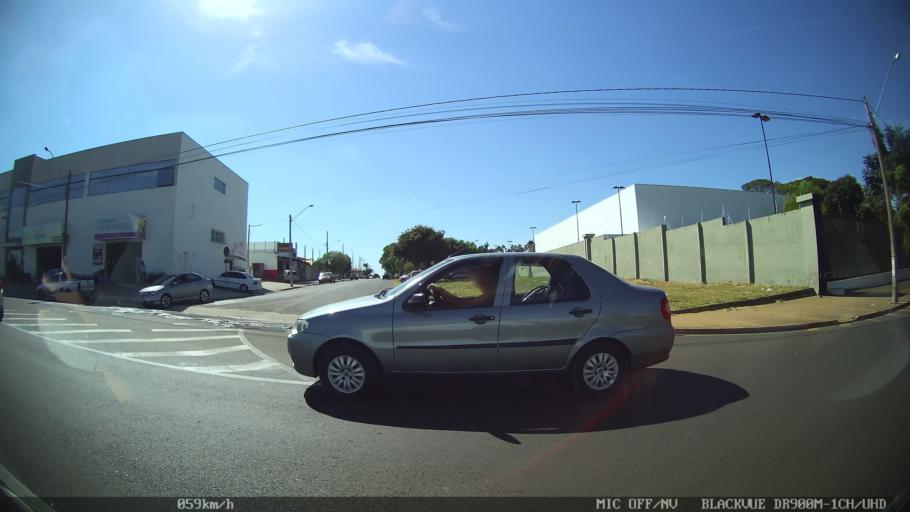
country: BR
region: Sao Paulo
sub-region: Franca
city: Franca
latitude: -20.5465
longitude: -47.4508
